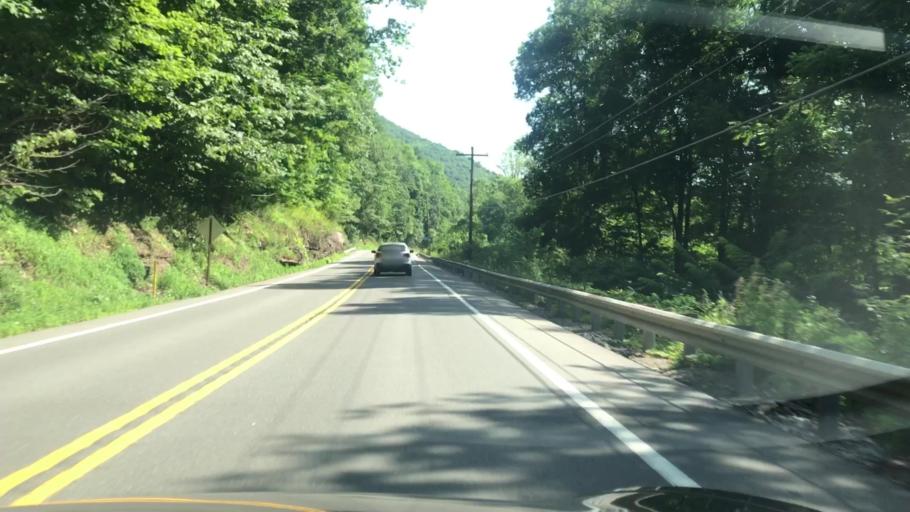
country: US
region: Pennsylvania
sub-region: Lycoming County
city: Garden View
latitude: 41.4301
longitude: -77.0084
